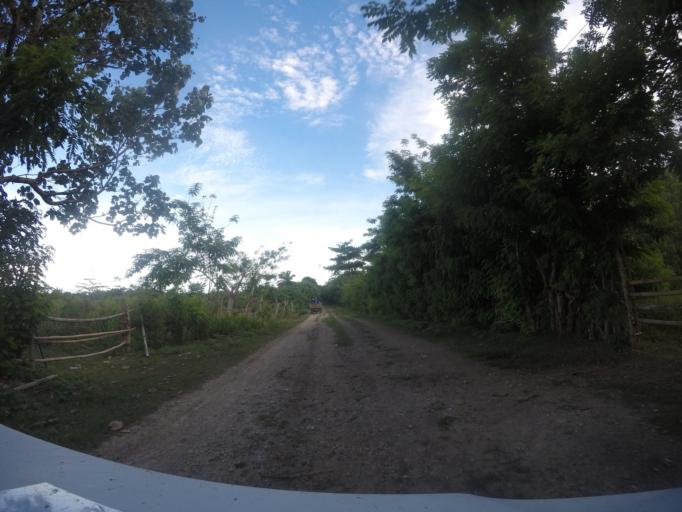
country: TL
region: Lautem
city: Lospalos
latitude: -8.5166
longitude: 126.9948
